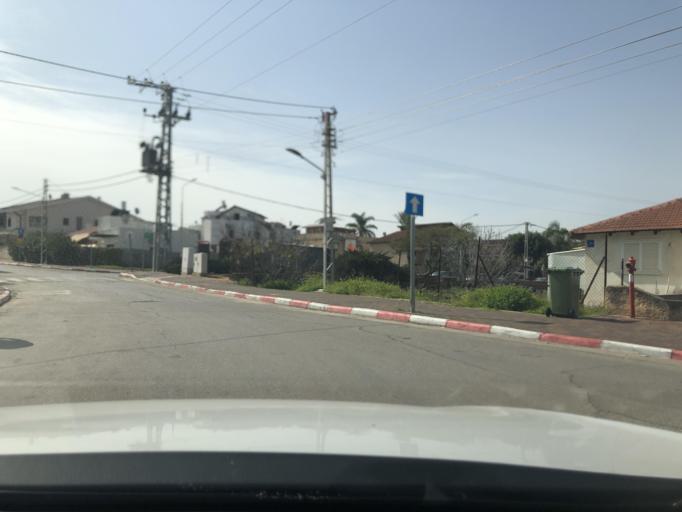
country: IL
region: Central District
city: Rosh Ha'Ayin
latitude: 32.0968
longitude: 34.9505
